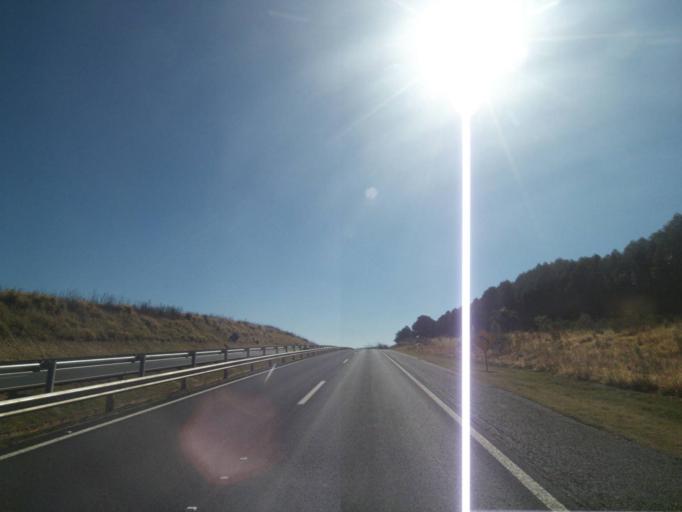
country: BR
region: Parana
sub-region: Tibagi
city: Tibagi
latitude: -24.8536
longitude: -50.4609
